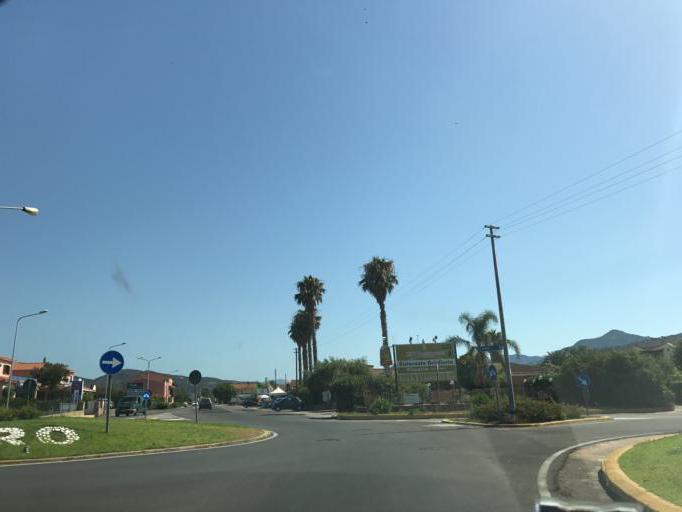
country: IT
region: Sardinia
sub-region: Provincia di Olbia-Tempio
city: San Teodoro
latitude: 40.7848
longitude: 9.6575
